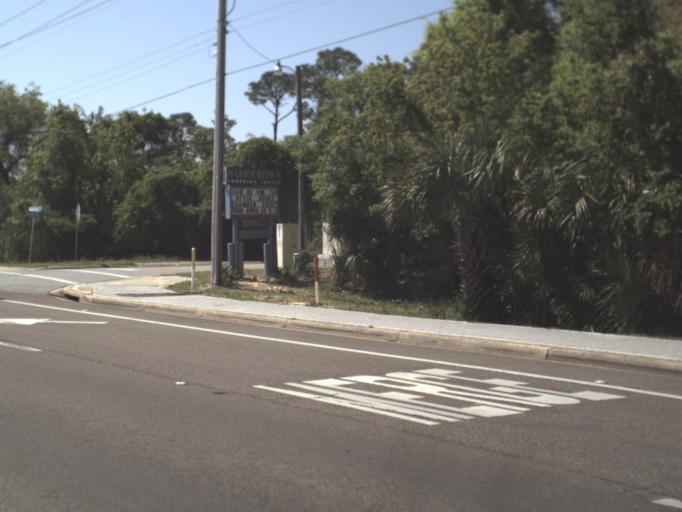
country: US
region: Florida
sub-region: Santa Rosa County
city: Gulf Breeze
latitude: 30.3557
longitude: -87.1588
